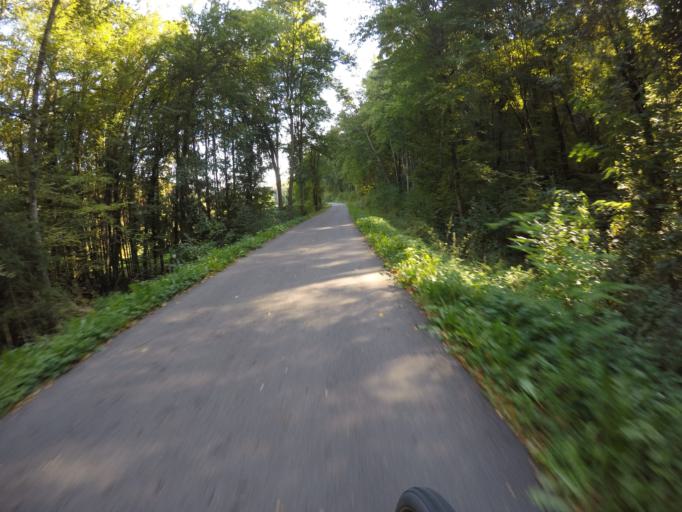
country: DE
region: Baden-Wuerttemberg
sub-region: Regierungsbezirk Stuttgart
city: Waldenbuch
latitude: 48.6510
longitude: 9.1581
